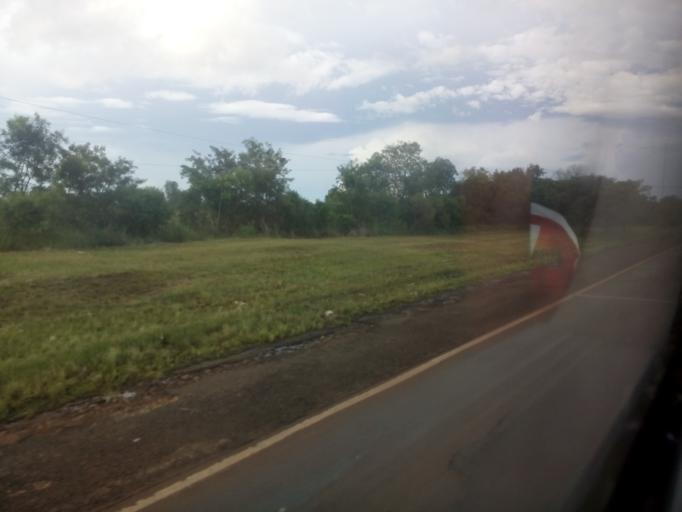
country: AR
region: Misiones
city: Santa Ana
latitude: -27.4298
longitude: -55.6321
